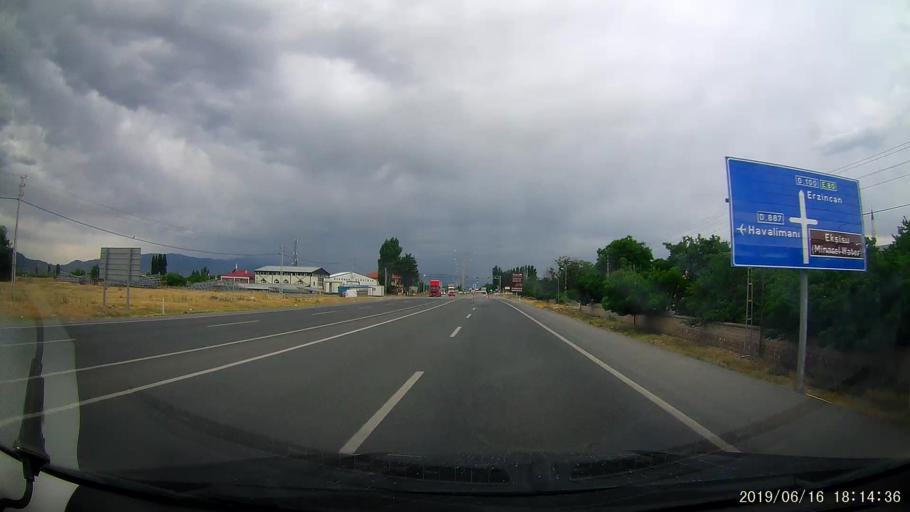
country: TR
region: Erzincan
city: Erzincan
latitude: 39.7252
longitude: 39.5558
